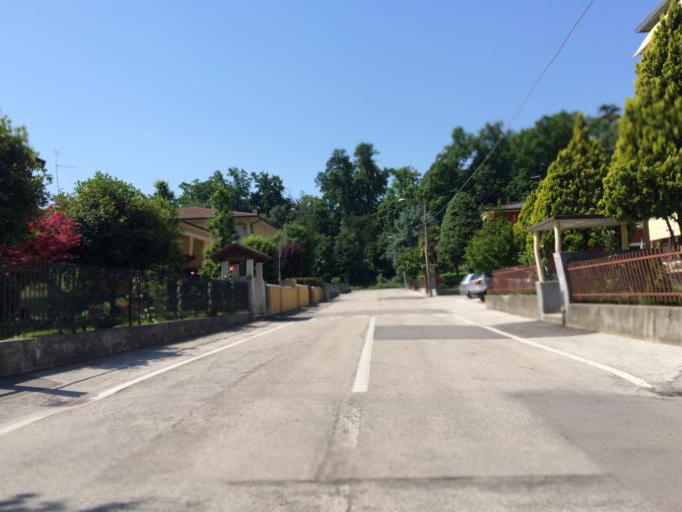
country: IT
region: Veneto
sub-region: Provincia di Vicenza
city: Montegalda
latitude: 45.4470
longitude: 11.6734
